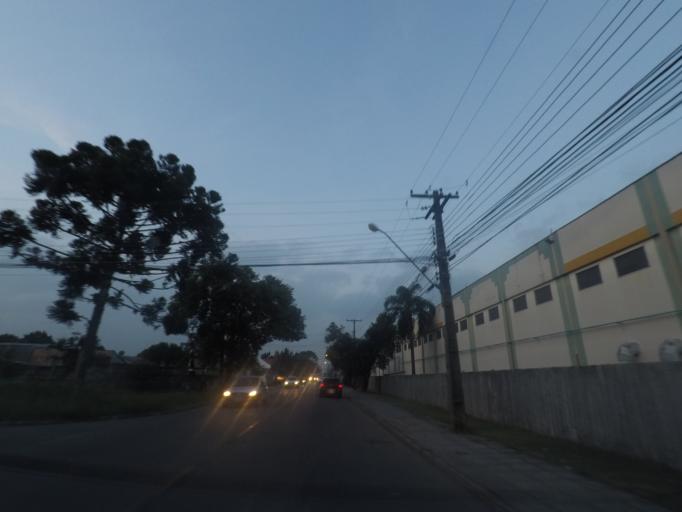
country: BR
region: Parana
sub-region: Pinhais
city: Pinhais
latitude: -25.4533
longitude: -49.1909
